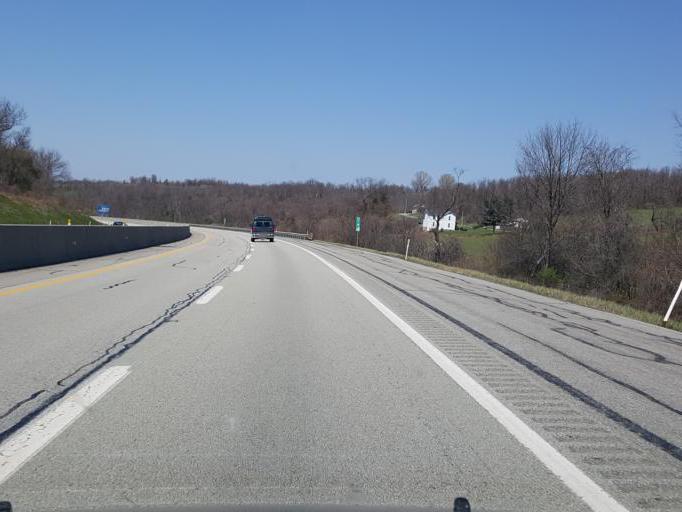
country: US
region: Pennsylvania
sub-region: Westmoreland County
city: Mount Pleasant
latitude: 40.1895
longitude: -79.5342
